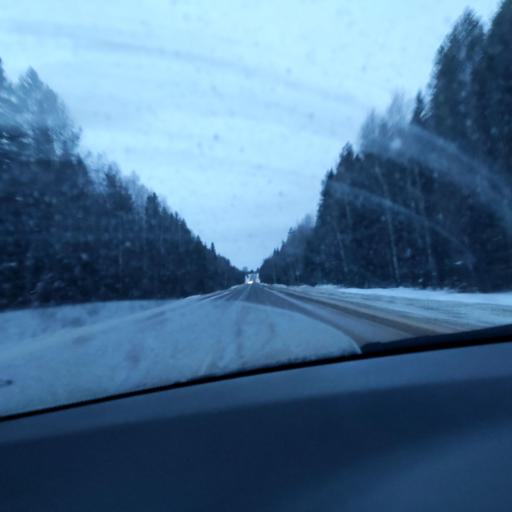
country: RU
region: Perm
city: Ust'-Kachka
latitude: 57.9104
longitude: 55.7732
